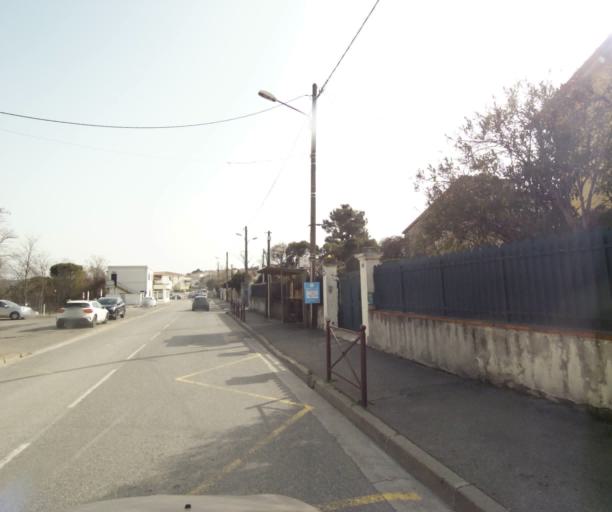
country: FR
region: Provence-Alpes-Cote d'Azur
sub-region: Departement des Bouches-du-Rhone
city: Marseille 15
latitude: 43.3815
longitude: 5.3467
